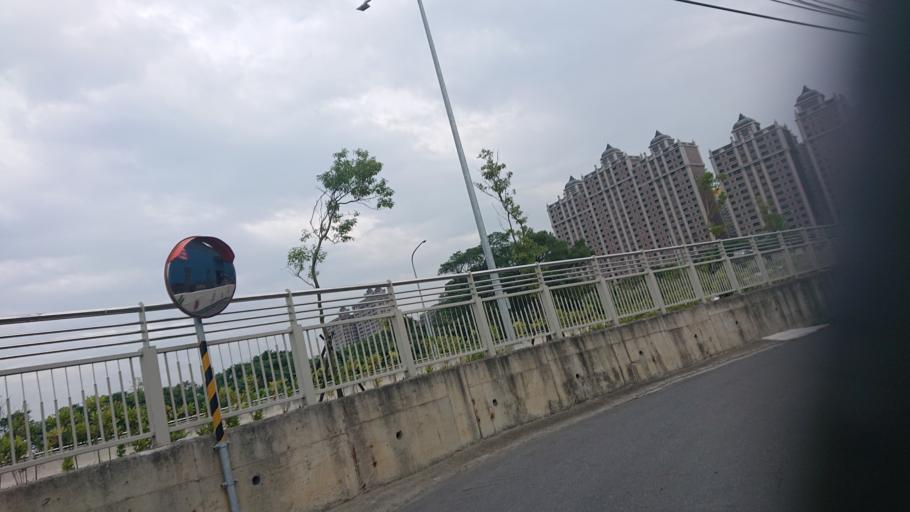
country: TW
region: Taiwan
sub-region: Taoyuan
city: Taoyuan
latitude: 24.9520
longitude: 121.3749
